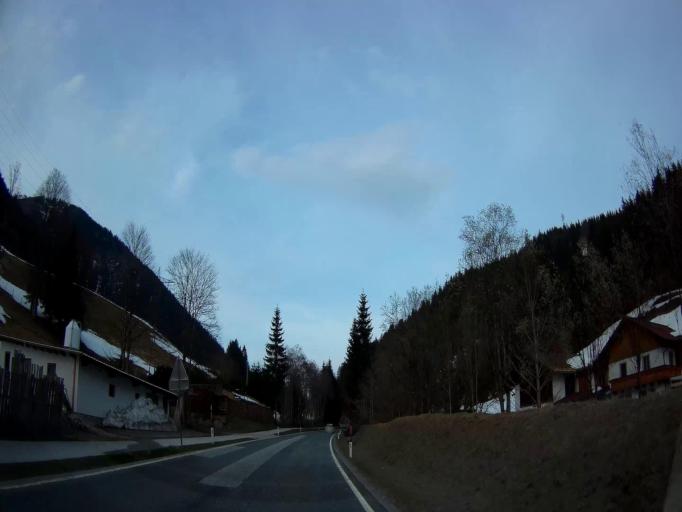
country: AT
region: Salzburg
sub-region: Politischer Bezirk Sankt Johann im Pongau
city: Eben im Pongau
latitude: 47.4489
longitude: 13.3651
